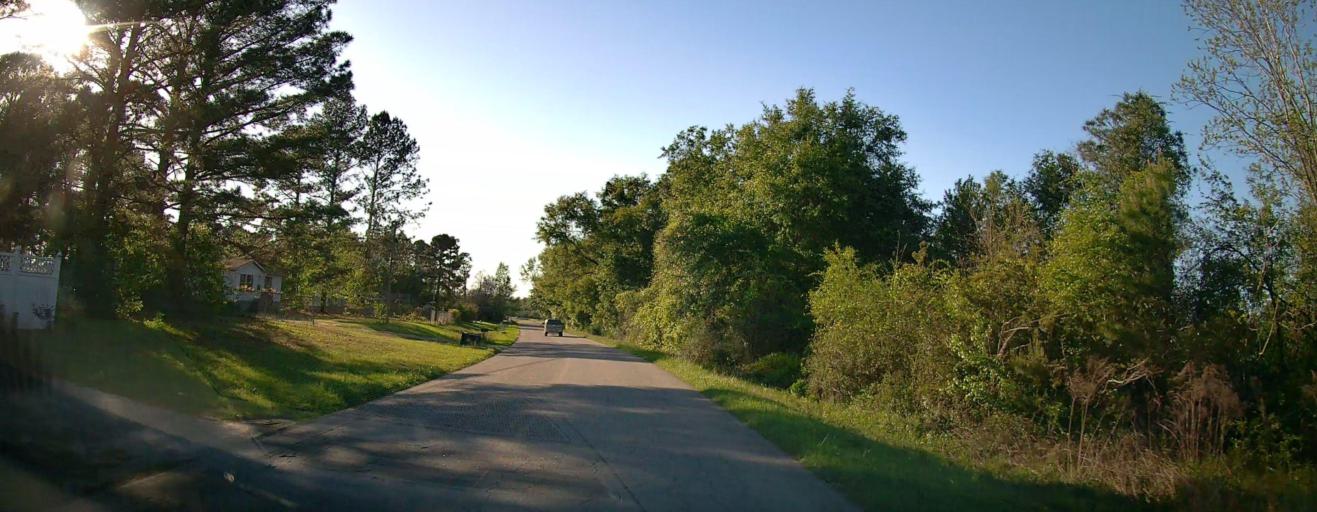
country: US
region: Georgia
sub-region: Ben Hill County
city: Fitzgerald
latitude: 31.7006
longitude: -83.2232
